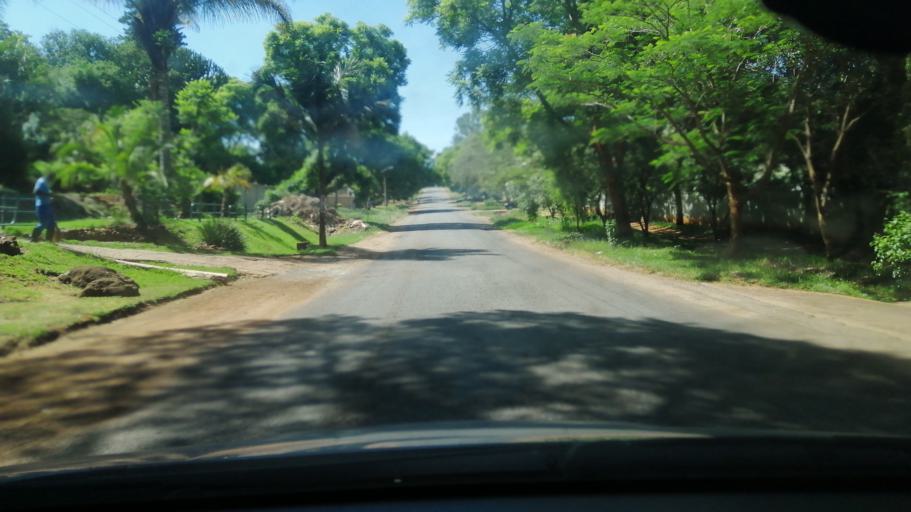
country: ZW
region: Harare
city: Harare
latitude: -17.7981
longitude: 31.1287
